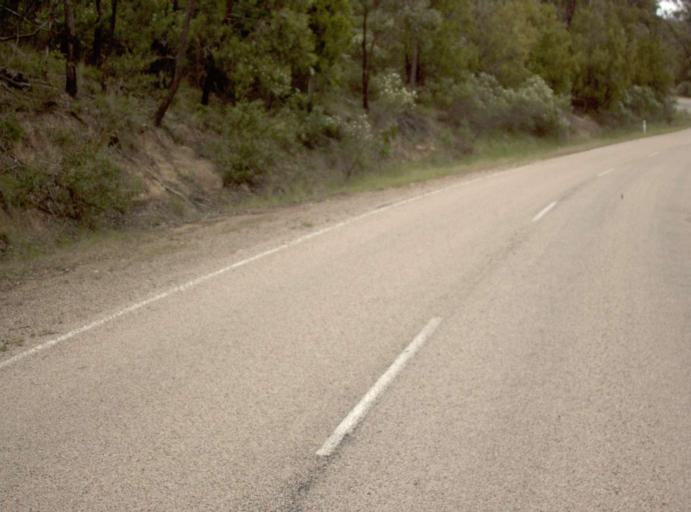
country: AU
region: Victoria
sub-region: East Gippsland
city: Bairnsdale
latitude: -37.6087
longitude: 147.1898
